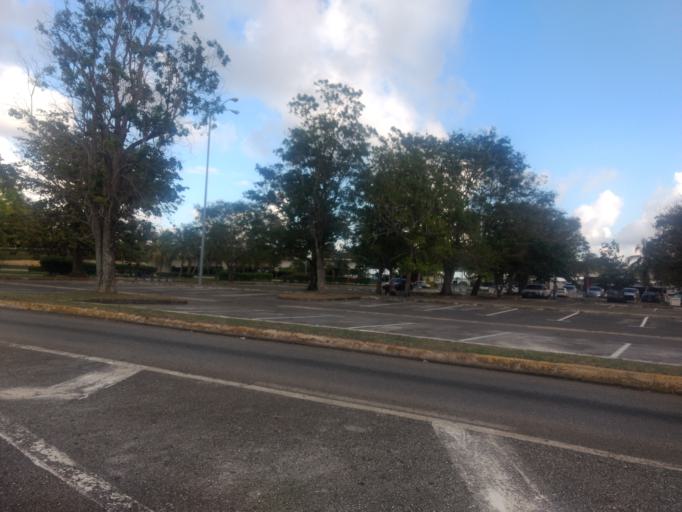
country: CU
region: La Habana
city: Boyeros
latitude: 22.9998
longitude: -82.4081
